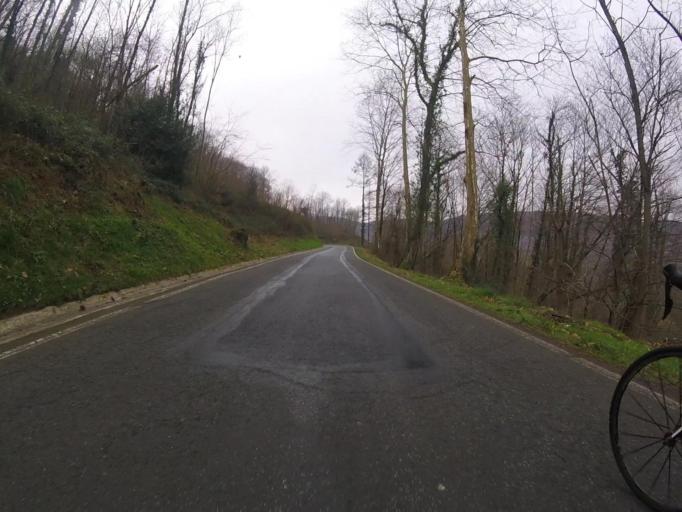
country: ES
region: Navarre
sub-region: Provincia de Navarra
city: Arantza
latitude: 43.2019
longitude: -1.7193
